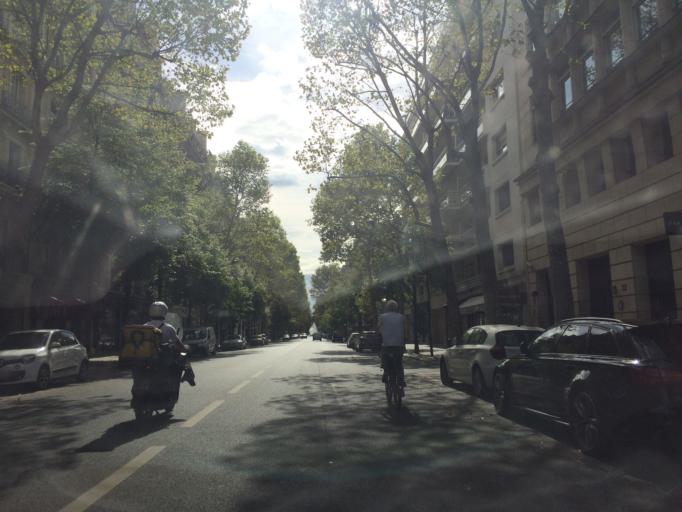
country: FR
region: Ile-de-France
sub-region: Departement des Hauts-de-Seine
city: Levallois-Perret
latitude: 48.8718
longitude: 2.2904
